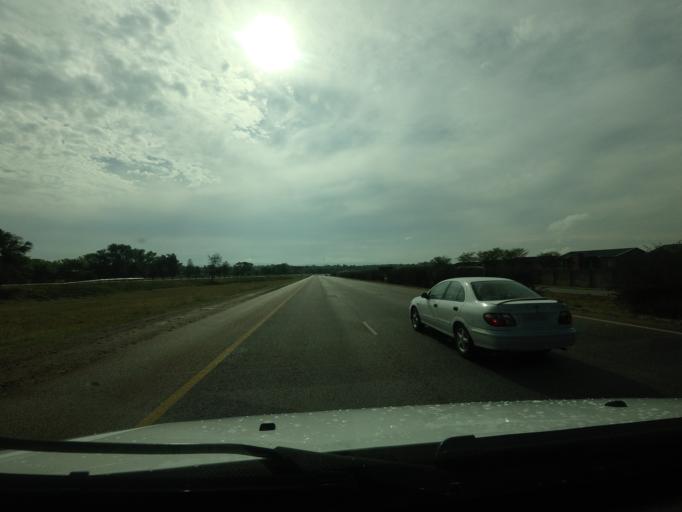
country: ZA
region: Gauteng
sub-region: City of Tshwane Metropolitan Municipality
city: Pretoria
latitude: -25.7520
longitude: 28.3289
